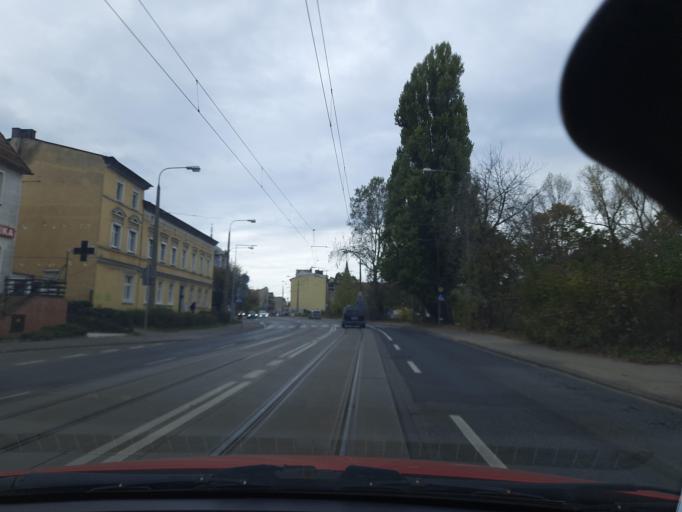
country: PL
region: Kujawsko-Pomorskie
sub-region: Bydgoszcz
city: Bydgoszcz
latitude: 53.1264
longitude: 17.9756
